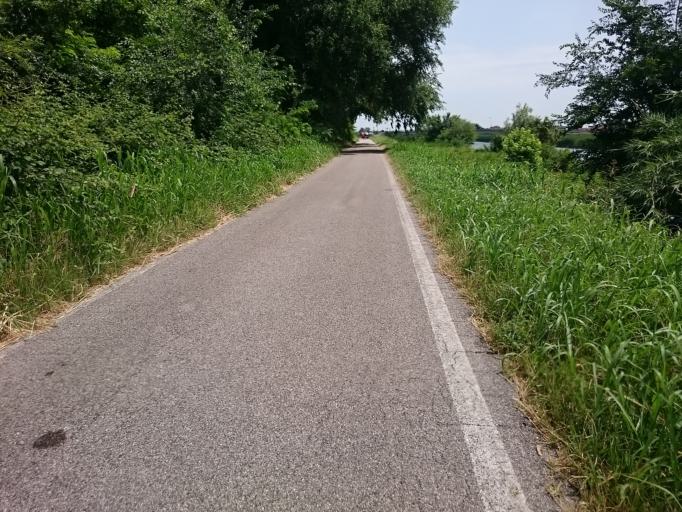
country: IT
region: Veneto
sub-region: Provincia di Venezia
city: Sant'Anna
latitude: 45.1852
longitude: 12.2371
